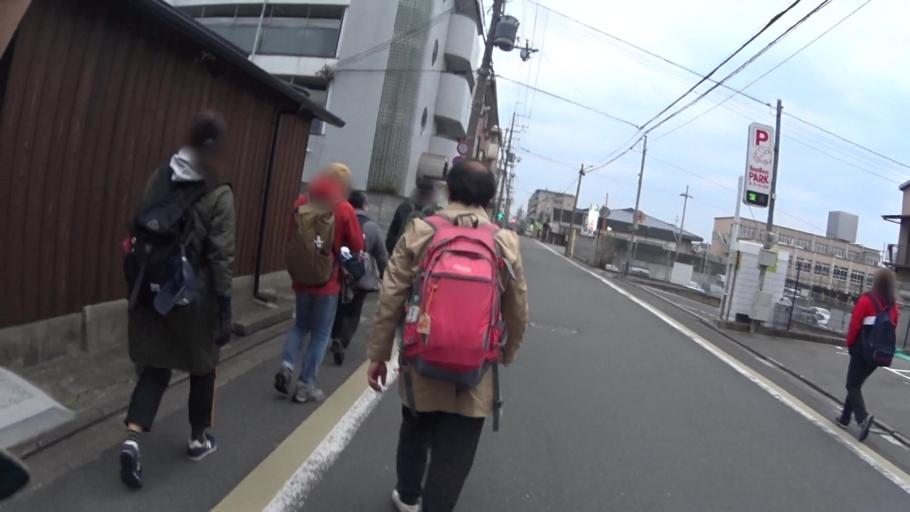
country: JP
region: Kyoto
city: Muko
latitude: 34.9396
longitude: 135.7623
